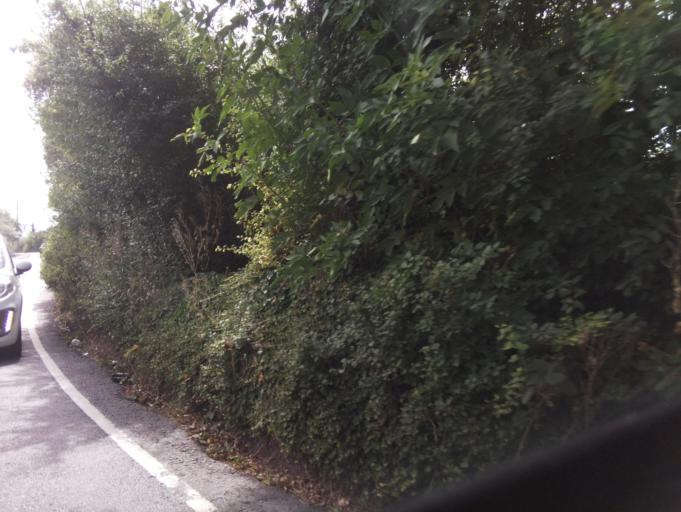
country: GB
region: England
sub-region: Bristol
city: Bristol
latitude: 51.4261
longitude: -2.5996
